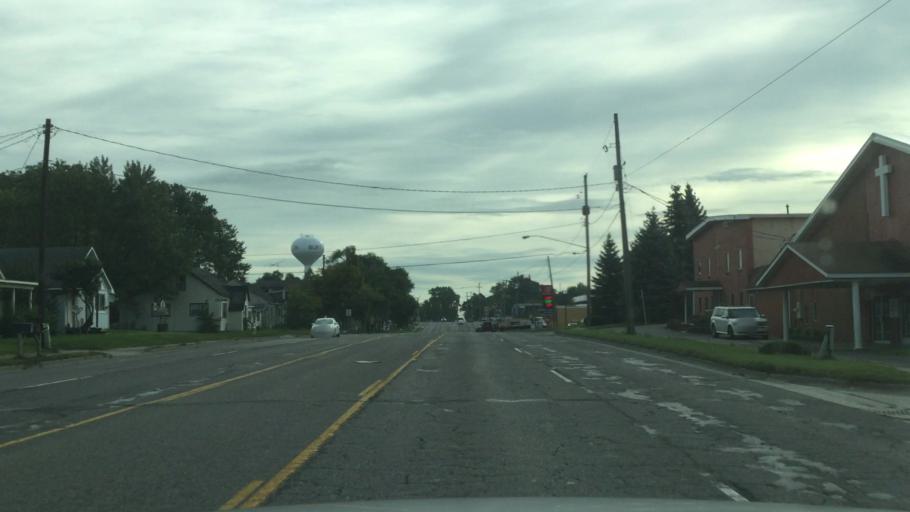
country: US
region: Michigan
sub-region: Genesee County
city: Flint
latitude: 42.9743
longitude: -83.6772
